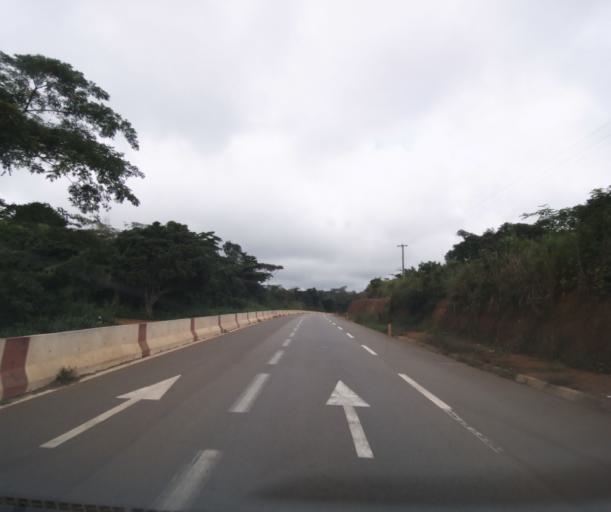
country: CM
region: Centre
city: Mbankomo
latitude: 3.7955
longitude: 11.3717
